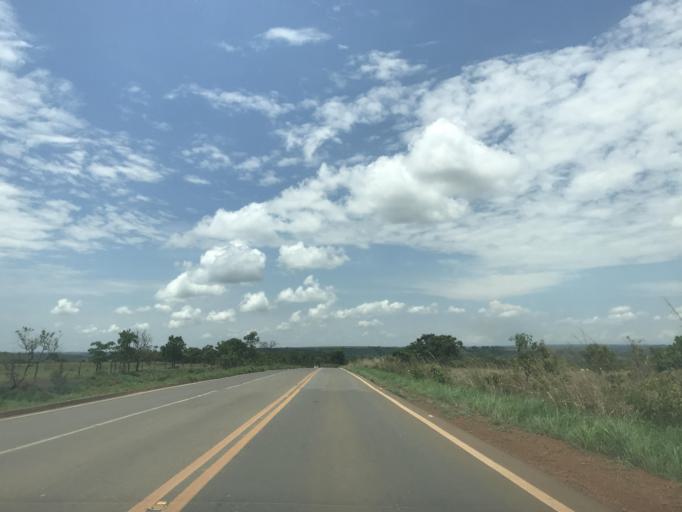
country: BR
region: Goias
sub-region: Luziania
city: Luziania
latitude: -16.3973
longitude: -48.1706
